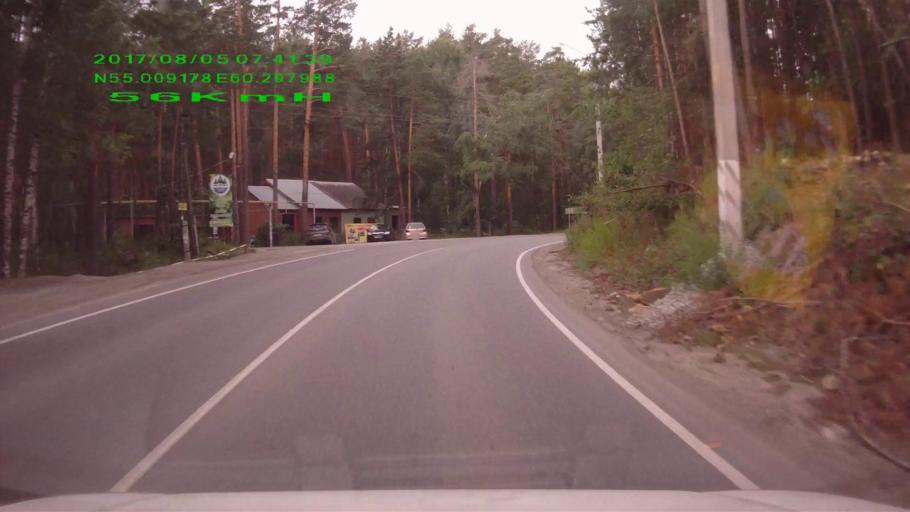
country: RU
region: Chelyabinsk
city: Chebarkul'
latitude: 55.0091
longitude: 60.2978
